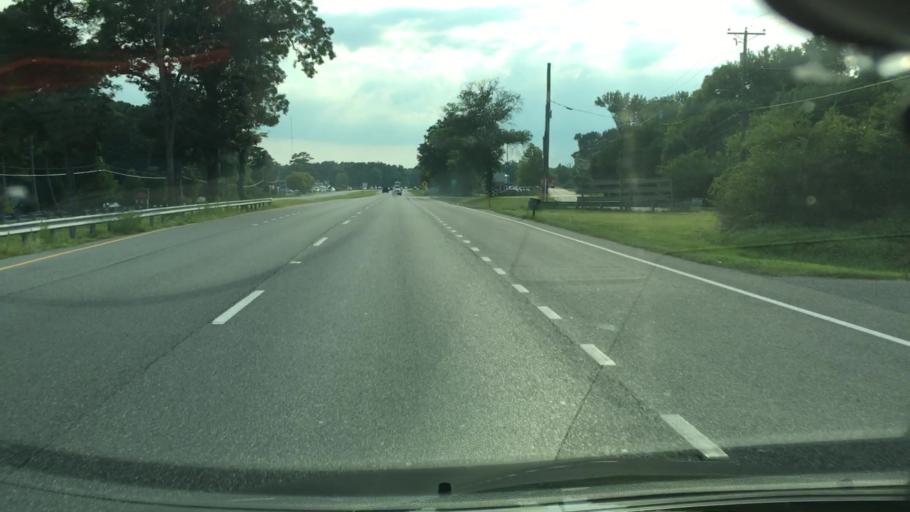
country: US
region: Maryland
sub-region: Worcester County
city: West Ocean City
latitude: 38.3383
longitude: -75.1365
